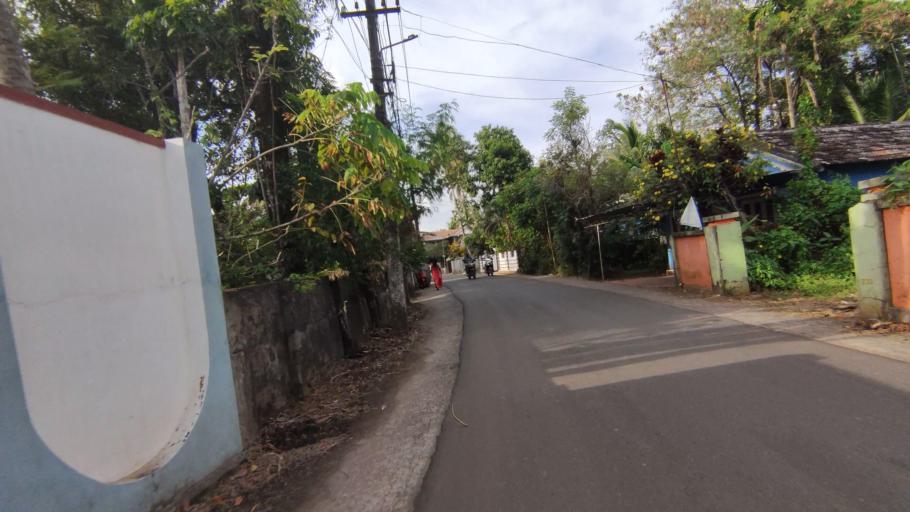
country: IN
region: Kerala
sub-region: Kottayam
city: Kottayam
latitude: 9.5831
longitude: 76.4990
